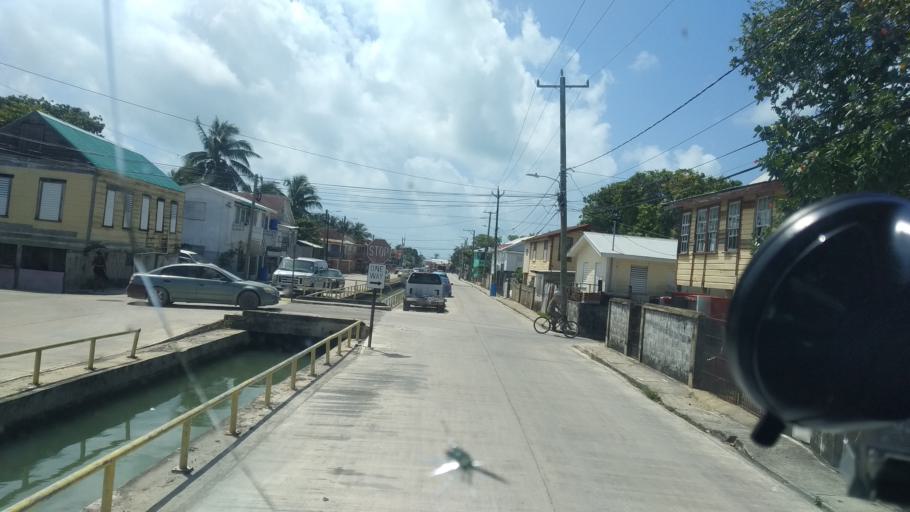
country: BZ
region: Belize
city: Belize City
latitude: 17.4921
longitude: -88.1893
